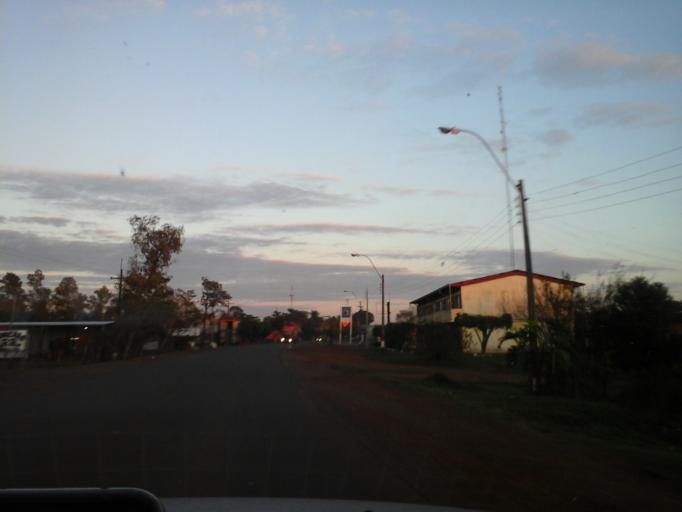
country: PY
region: Itapua
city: General Delgado
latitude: -27.0903
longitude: -56.5189
